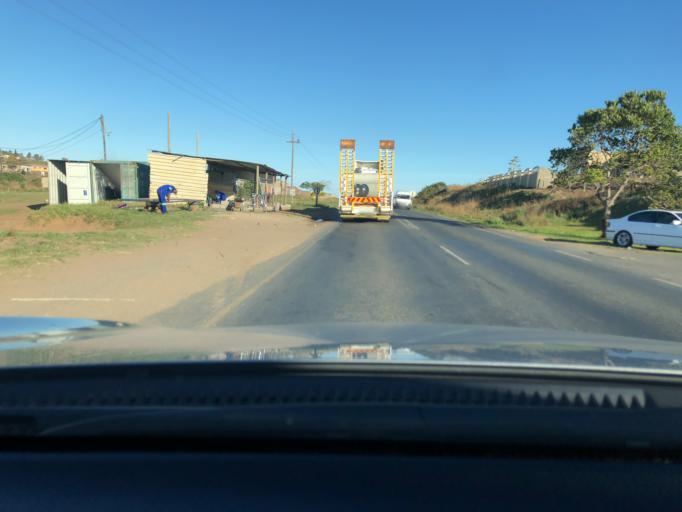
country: ZA
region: KwaZulu-Natal
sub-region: eThekwini Metropolitan Municipality
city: Umkomaas
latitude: -30.0080
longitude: 30.8036
